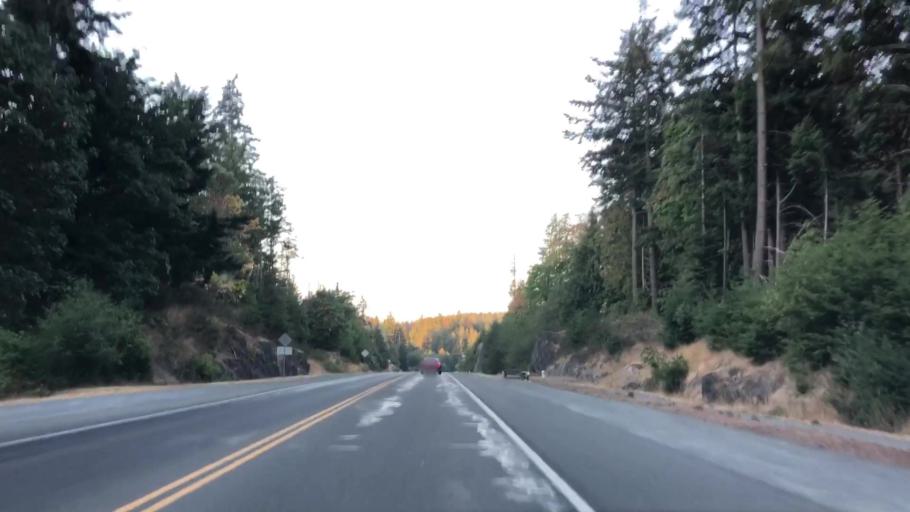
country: CA
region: British Columbia
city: Colwood
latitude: 48.4136
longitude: -123.5052
